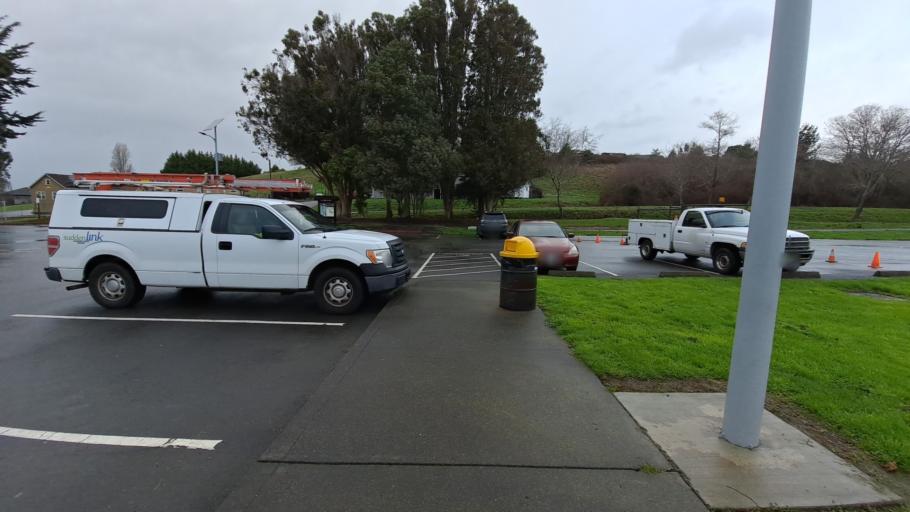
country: US
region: California
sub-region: Humboldt County
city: Fortuna
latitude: 40.5931
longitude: -124.1367
